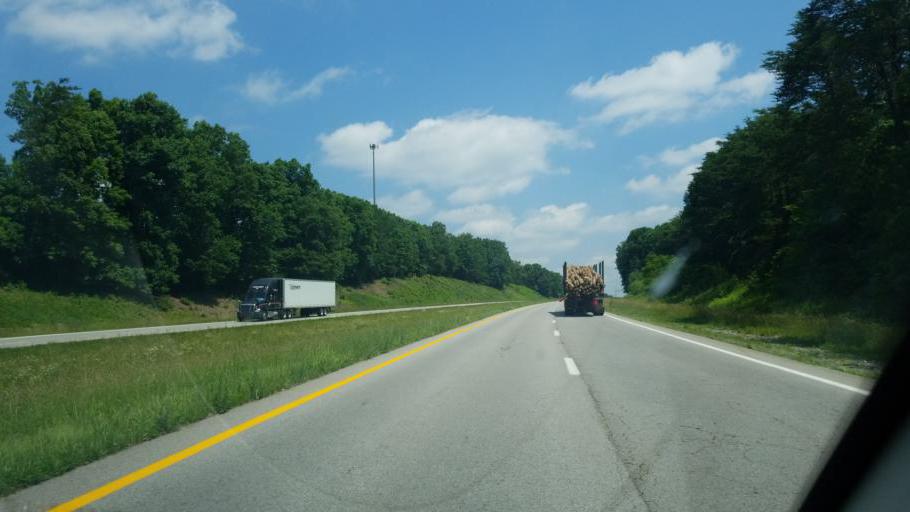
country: US
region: Virginia
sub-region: Pittsylvania County
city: Hurt
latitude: 37.1068
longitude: -79.3315
